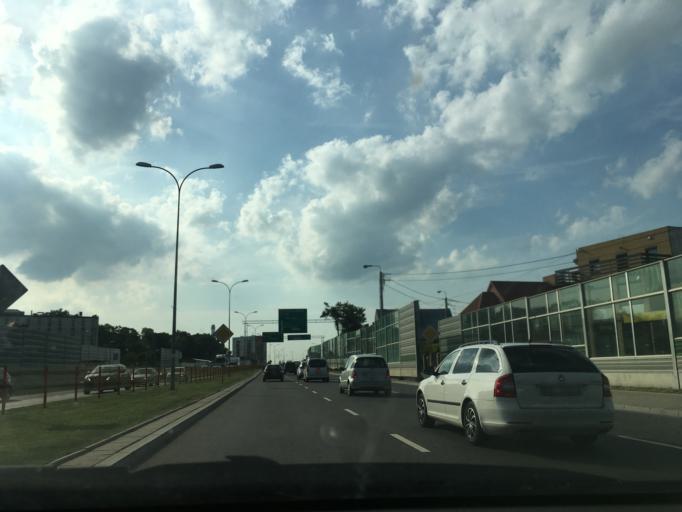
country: PL
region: Podlasie
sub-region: Bialystok
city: Bialystok
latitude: 53.1440
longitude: 23.1891
